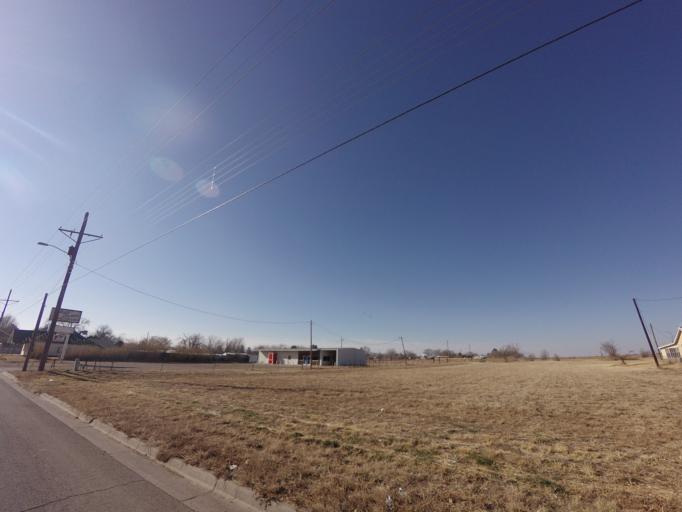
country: US
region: New Mexico
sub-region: Curry County
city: Clovis
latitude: 34.3832
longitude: -103.1966
